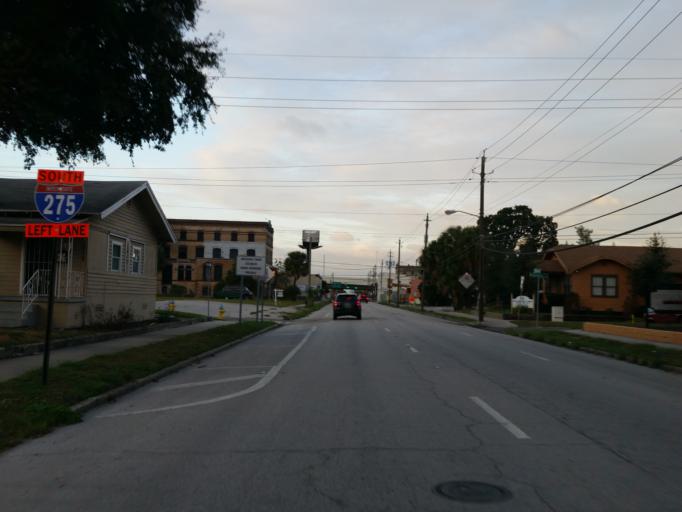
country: US
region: Florida
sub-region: Hillsborough County
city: Tampa
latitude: 27.9524
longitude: -82.4830
